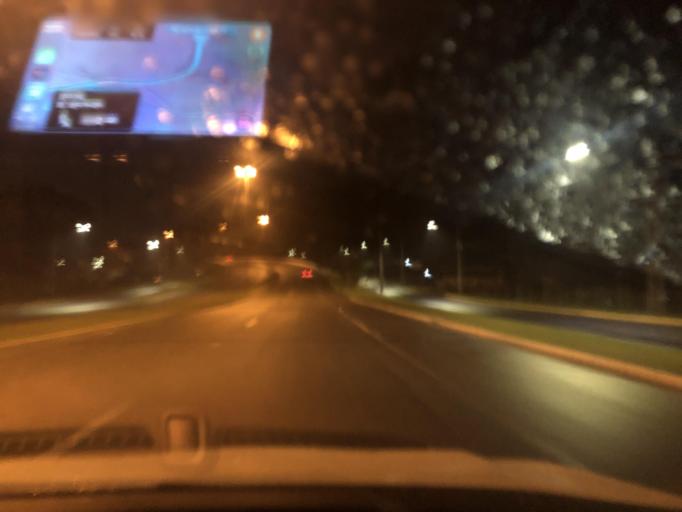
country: BR
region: Santa Catarina
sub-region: Joinville
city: Joinville
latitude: -26.3744
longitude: -48.8354
